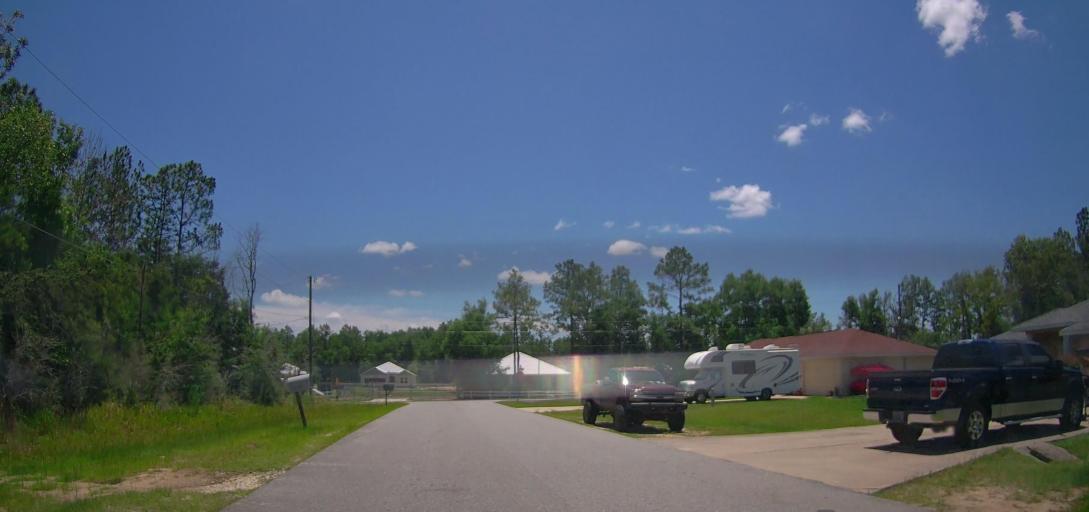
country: US
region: Florida
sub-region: Marion County
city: Silver Springs Shores
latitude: 29.1376
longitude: -82.0218
